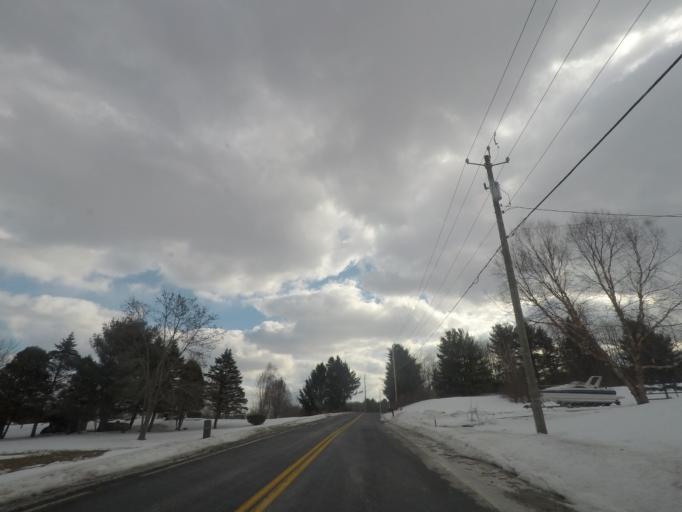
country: US
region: New York
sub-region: Saratoga County
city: Mechanicville
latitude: 42.9171
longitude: -73.7431
